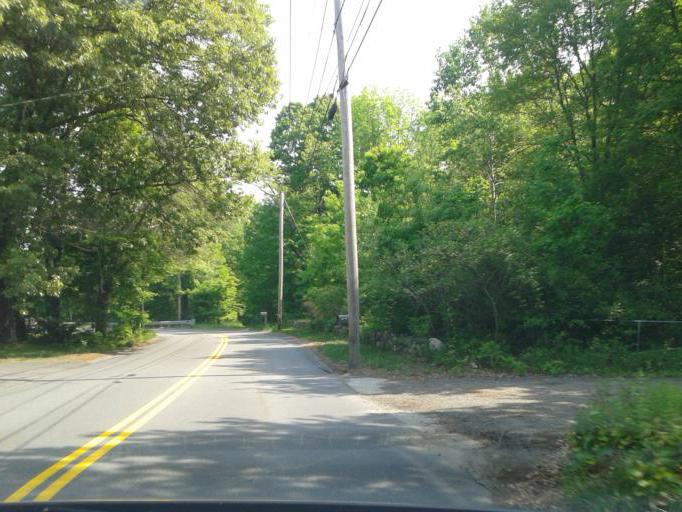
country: US
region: Massachusetts
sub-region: Worcester County
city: Westborough
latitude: 42.2680
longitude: -71.6334
